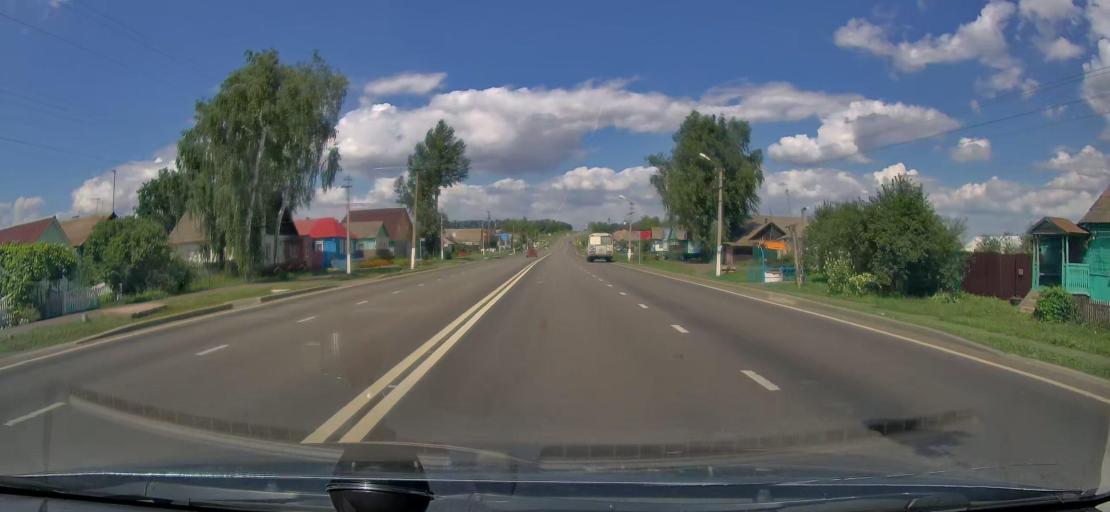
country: RU
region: Kursk
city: Zolotukhino
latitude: 51.9475
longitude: 36.3044
